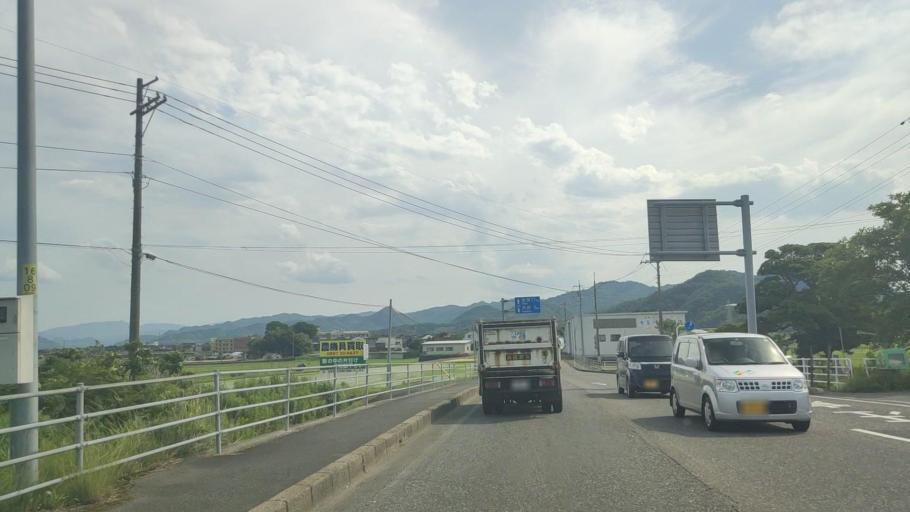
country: JP
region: Tottori
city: Tottori
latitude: 35.4800
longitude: 134.2077
